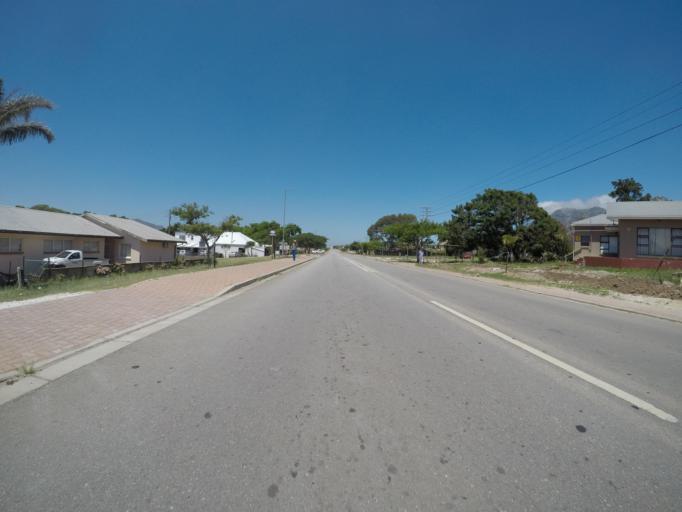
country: ZA
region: Eastern Cape
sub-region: Cacadu District Municipality
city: Kareedouw
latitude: -33.9516
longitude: 24.2891
